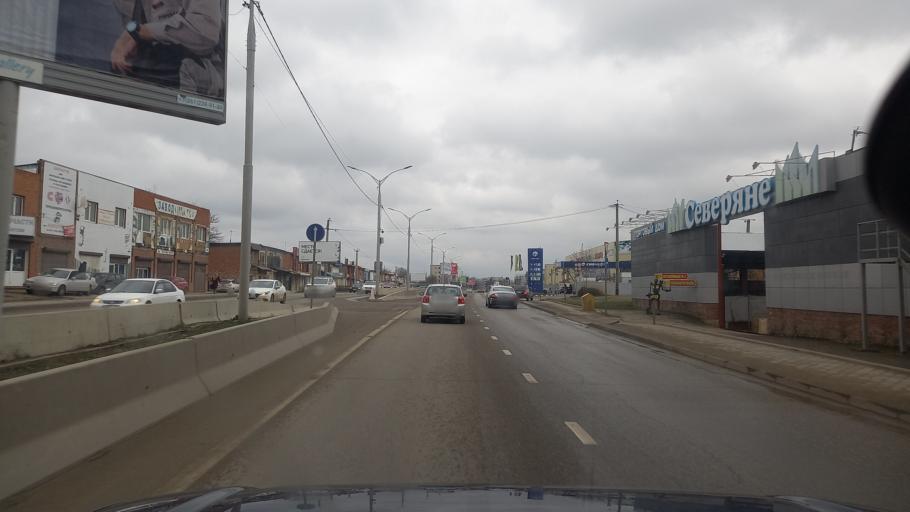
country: RU
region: Krasnodarskiy
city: Pashkovskiy
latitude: 45.0438
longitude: 39.1148
